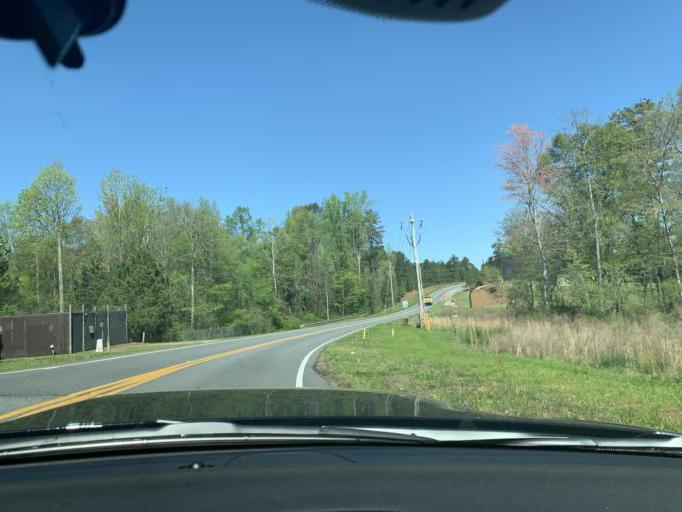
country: US
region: Georgia
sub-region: Fulton County
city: Milton
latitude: 34.1227
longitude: -84.2078
